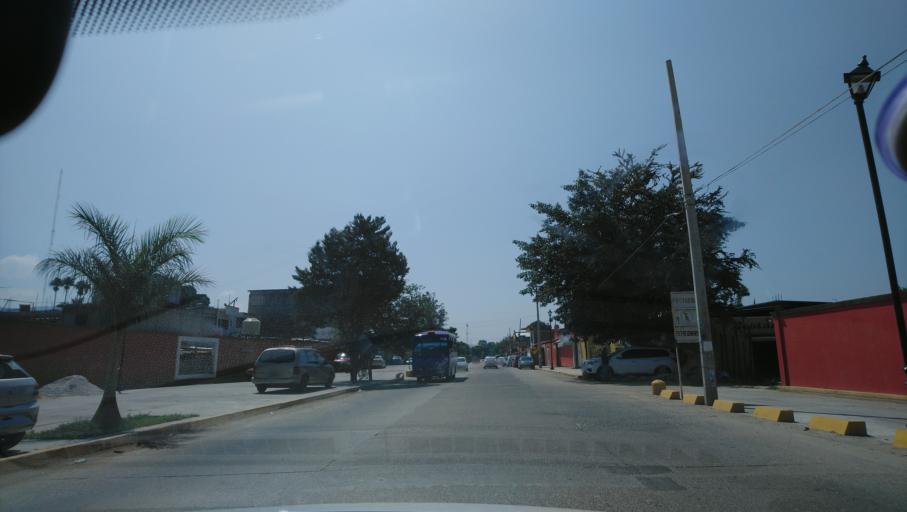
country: MX
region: Oaxaca
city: Santa Maria del Tule
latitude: 17.0461
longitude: -96.6385
